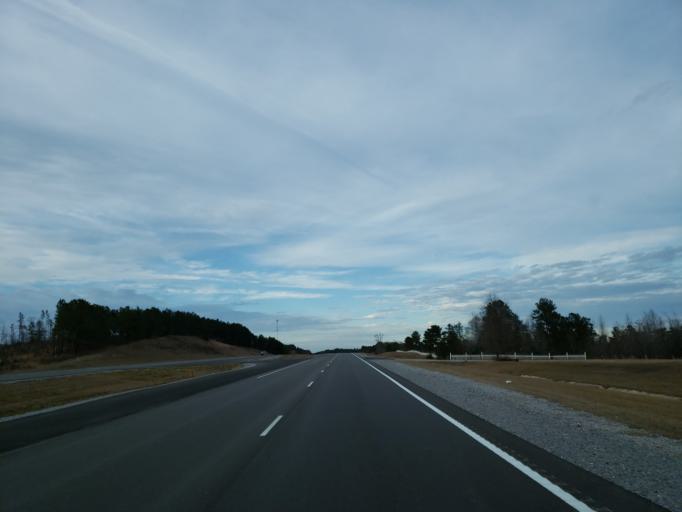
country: US
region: Mississippi
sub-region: Clarke County
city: Stonewall
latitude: 32.1192
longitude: -88.7158
